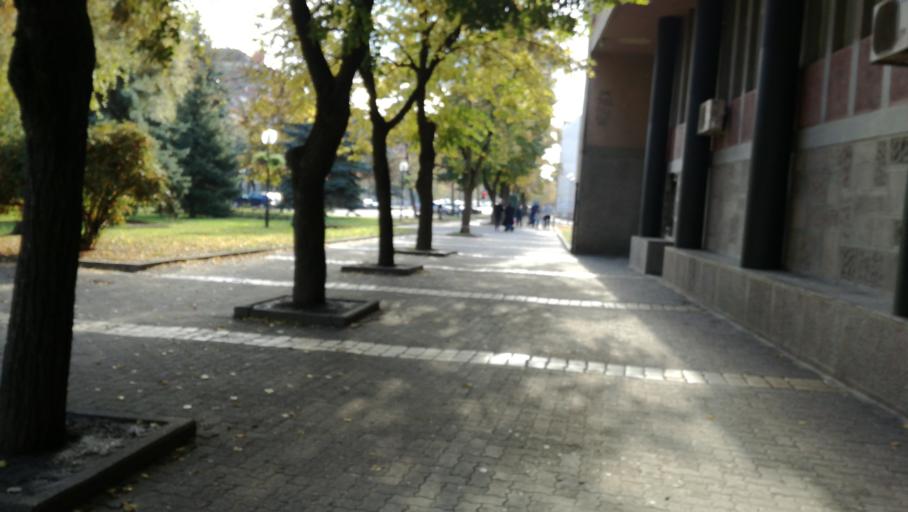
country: RS
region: Autonomna Pokrajina Vojvodina
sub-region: Severnobanatski Okrug
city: Kikinda
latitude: 45.8294
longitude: 20.4639
